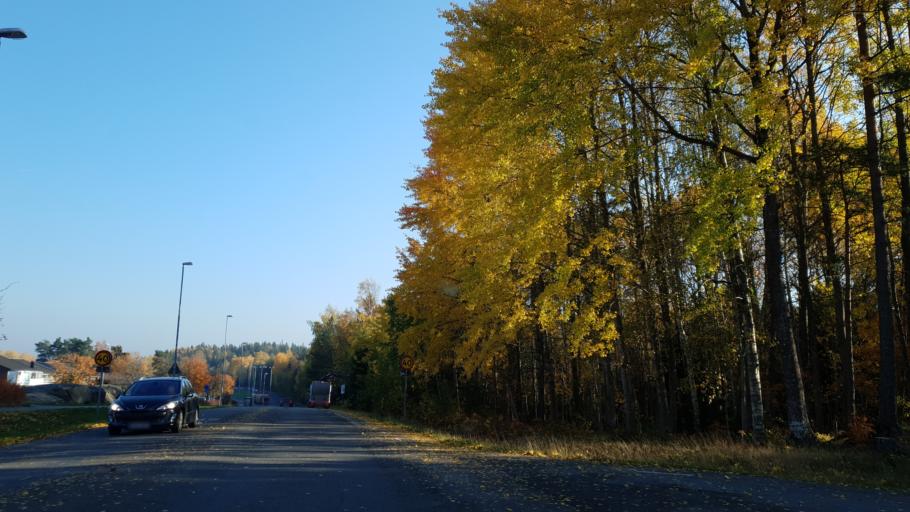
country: SE
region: Stockholm
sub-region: Haninge Kommun
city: Haninge
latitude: 59.1697
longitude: 18.1944
